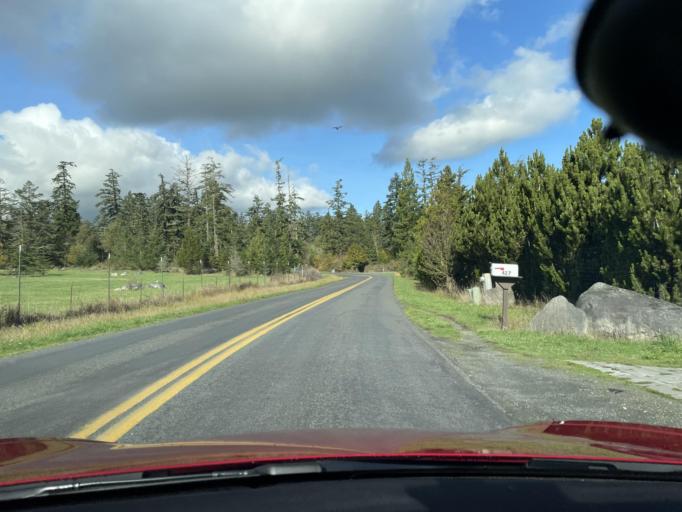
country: US
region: Washington
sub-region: San Juan County
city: Friday Harbor
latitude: 48.5061
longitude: -123.0206
